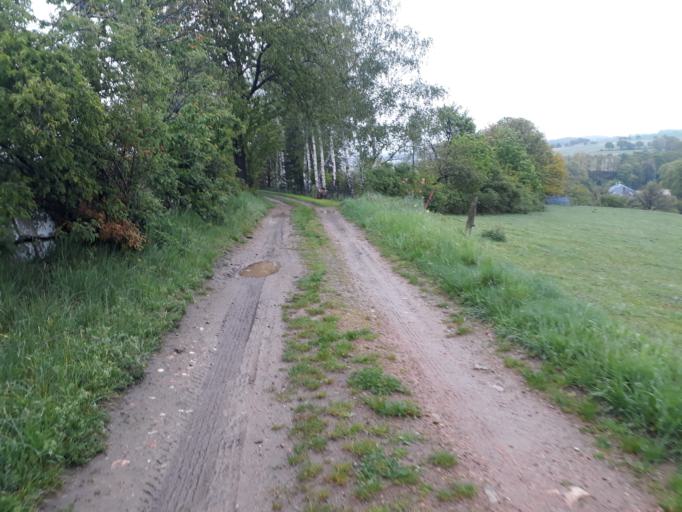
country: DE
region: Saxony
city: Reinhardtsgrimma
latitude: 50.8919
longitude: 13.7439
